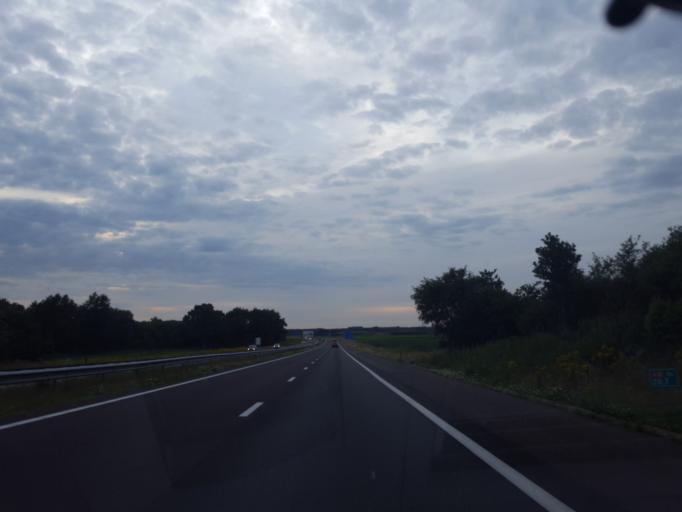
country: NL
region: Overijssel
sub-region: Gemeente Steenwijkerland
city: Steenwijk
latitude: 52.7894
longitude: 6.1558
